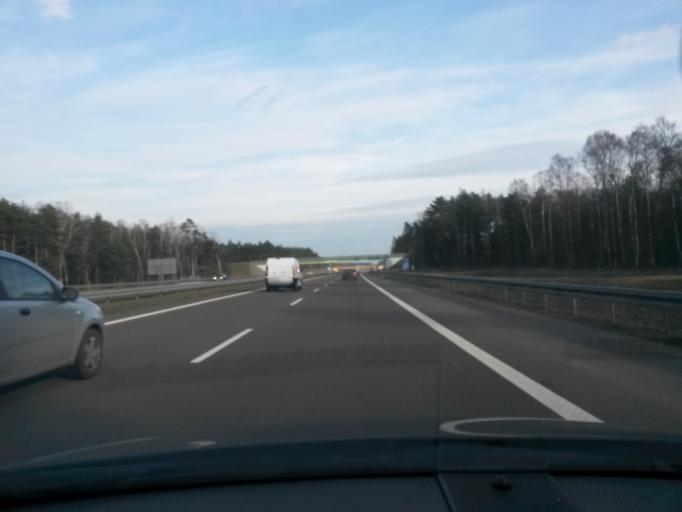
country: PL
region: Lodz Voivodeship
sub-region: Powiat zgierski
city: Zgierz
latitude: 51.9132
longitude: 19.4303
